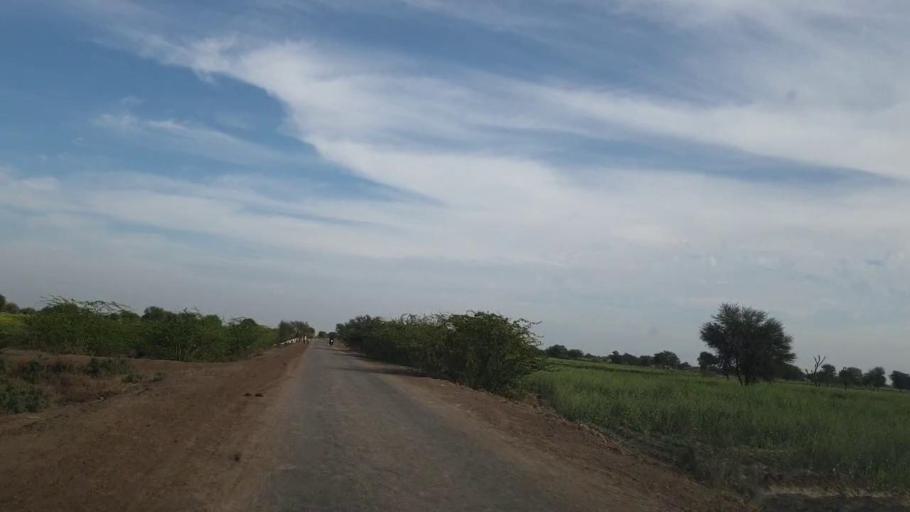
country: PK
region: Sindh
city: Pithoro
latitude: 25.6336
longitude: 69.3980
